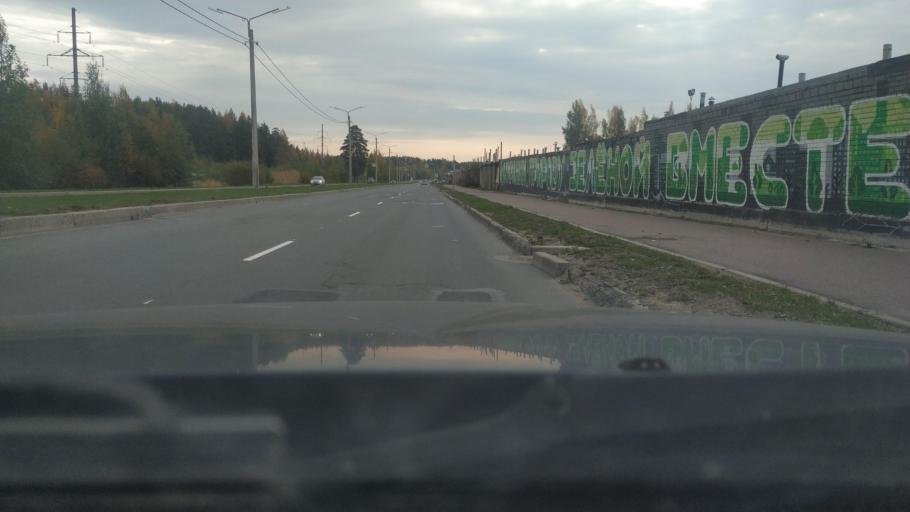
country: RU
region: Leningrad
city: Sosnovyy Bor
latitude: 59.9071
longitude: 29.1035
